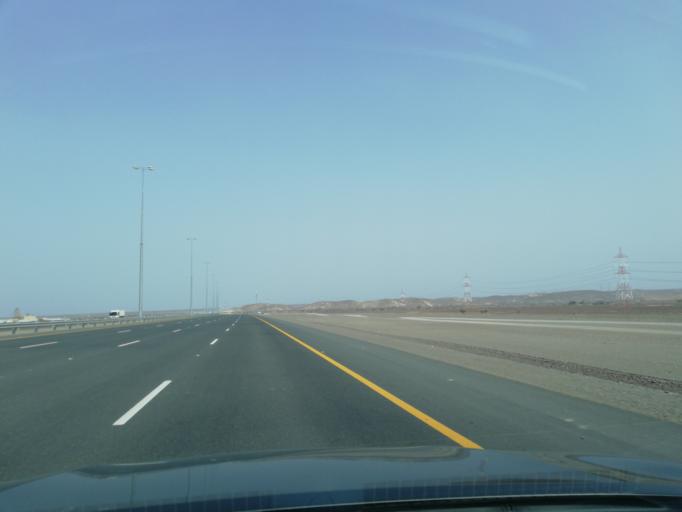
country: OM
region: Al Batinah
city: Al Sohar
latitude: 24.3094
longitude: 56.5886
